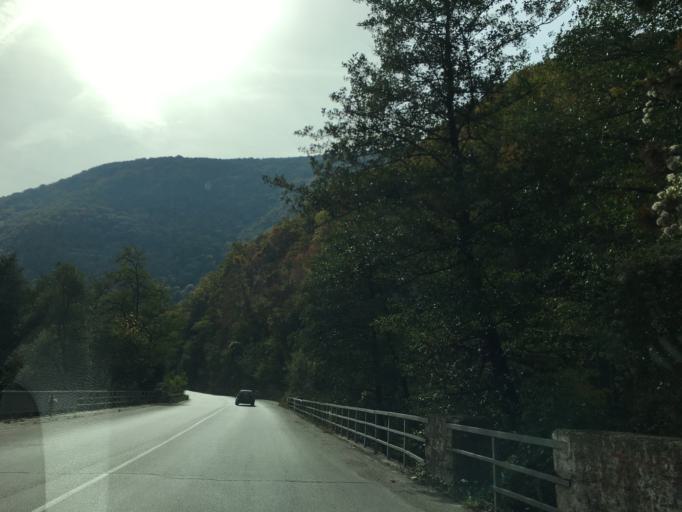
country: BG
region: Sofia-Capital
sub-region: Stolichna Obshtina
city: Sofia
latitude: 42.5603
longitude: 23.4225
